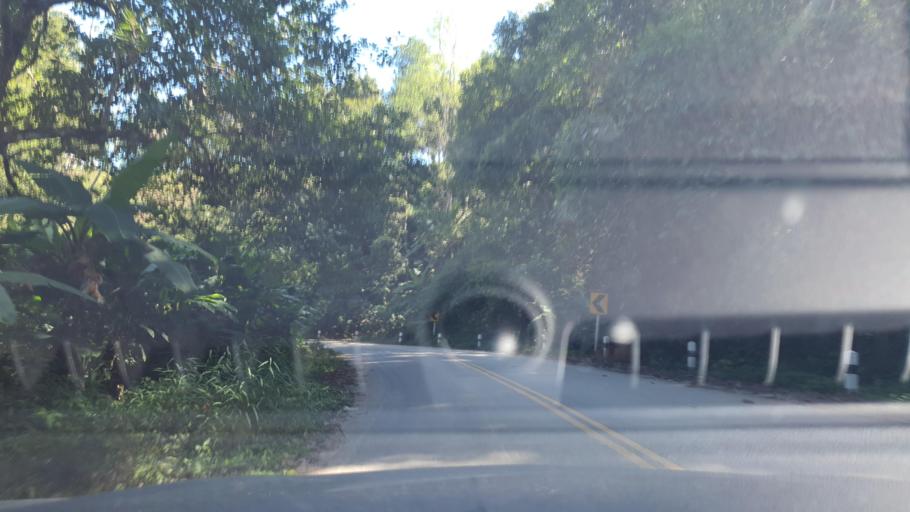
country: TH
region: Chiang Mai
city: Phrao
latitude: 19.3125
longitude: 99.3311
